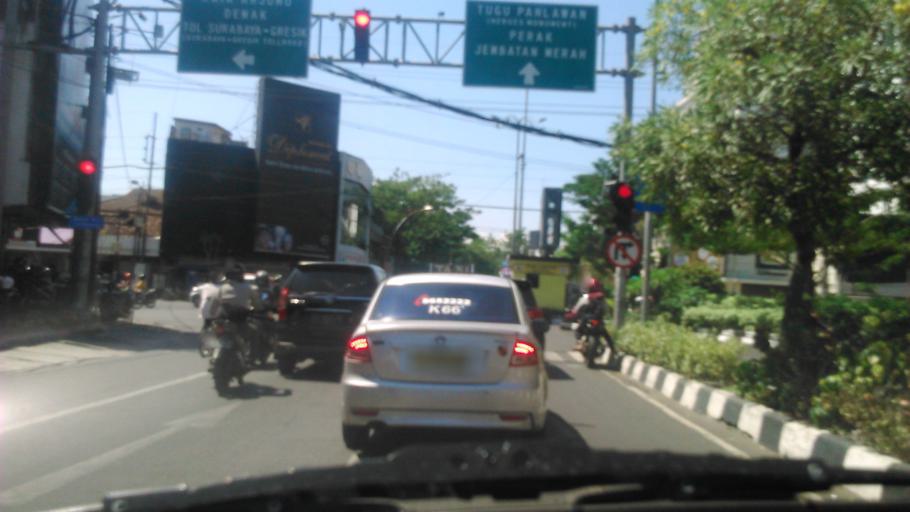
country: ID
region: East Java
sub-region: Kota Surabaya
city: Surabaya
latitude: -7.2589
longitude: 112.7330
